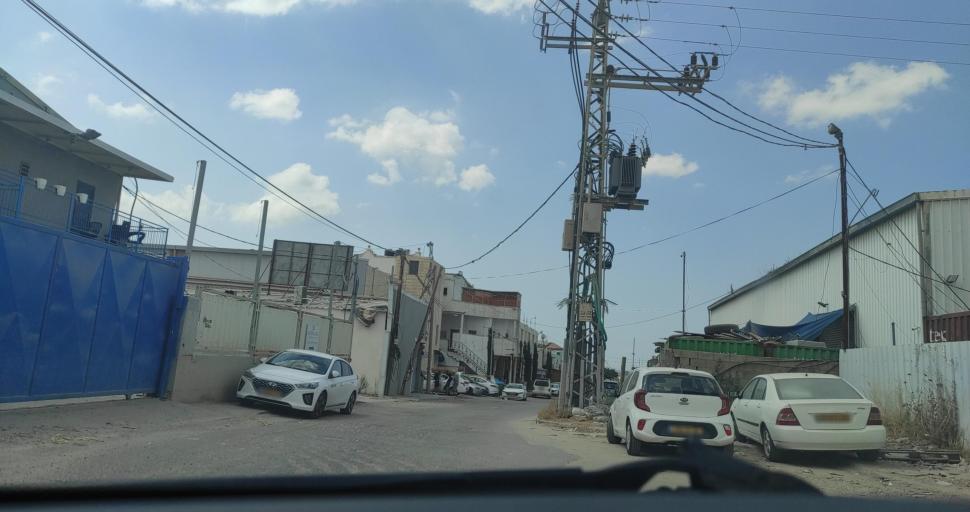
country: IL
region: Central District
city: Kafr Qasim
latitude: 32.1163
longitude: 34.9575
